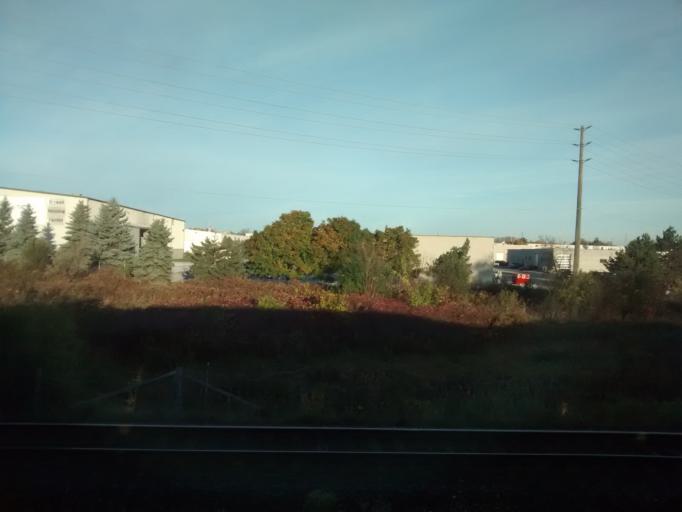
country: CA
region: Ontario
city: Oakville
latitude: 43.4152
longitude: -79.7241
